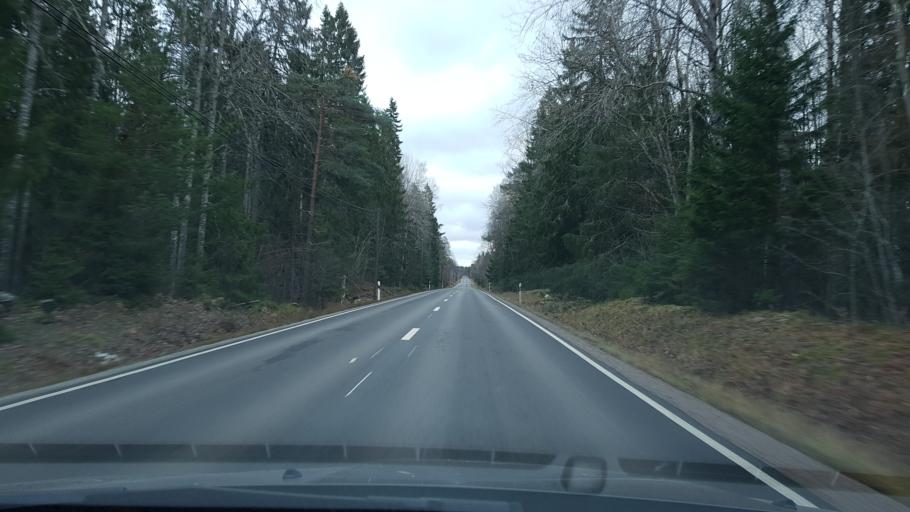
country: SE
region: Stockholm
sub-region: Norrtalje Kommun
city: Skanninge
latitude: 60.0177
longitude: 18.3629
